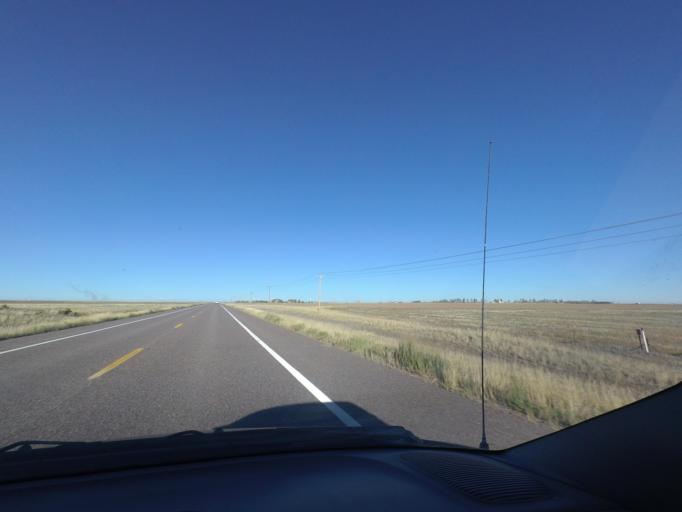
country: US
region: Colorado
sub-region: Arapahoe County
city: Byers
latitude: 39.7396
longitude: -104.1469
